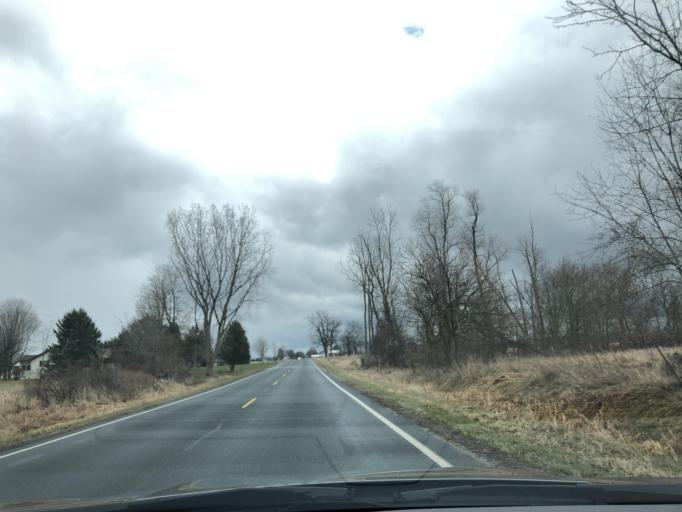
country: US
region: Michigan
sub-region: Clinton County
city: Saint Johns
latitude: 43.0462
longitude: -84.6274
